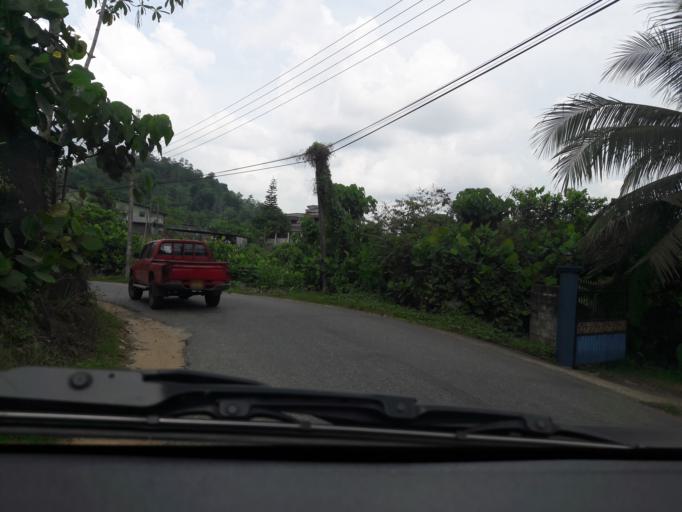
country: LK
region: Southern
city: Hikkaduwa
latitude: 6.2490
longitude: 80.2685
